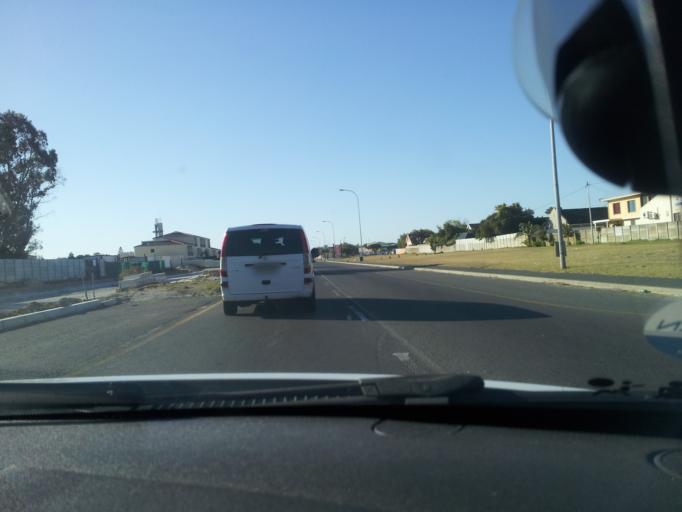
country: ZA
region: Western Cape
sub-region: Cape Winelands District Municipality
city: Stellenbosch
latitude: -34.1028
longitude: 18.8324
